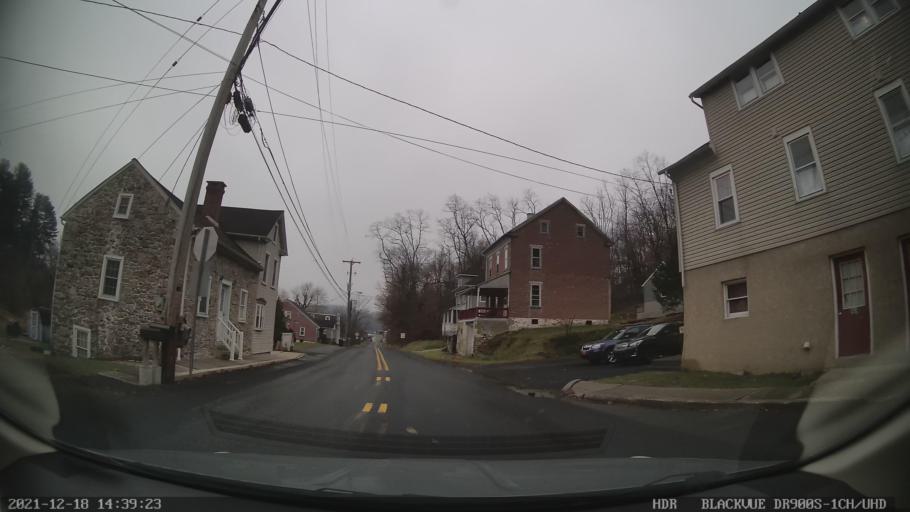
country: US
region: Pennsylvania
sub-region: Berks County
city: New Berlinville
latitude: 40.3748
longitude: -75.6335
